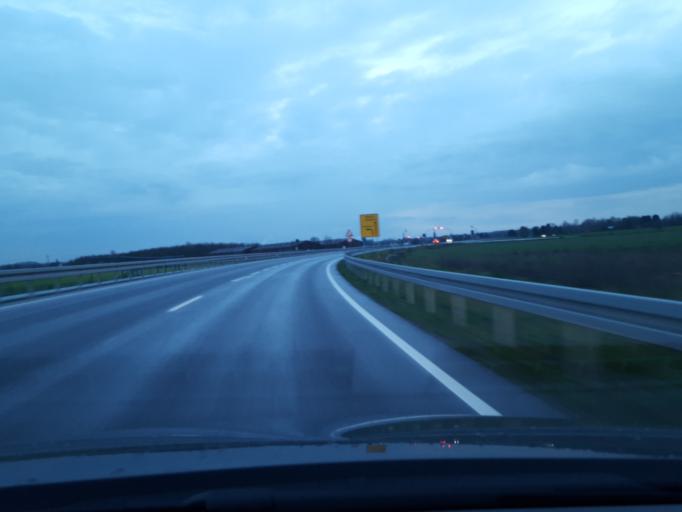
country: DE
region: North Rhine-Westphalia
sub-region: Regierungsbezirk Koln
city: Troisdorf
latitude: 50.7907
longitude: 7.1019
